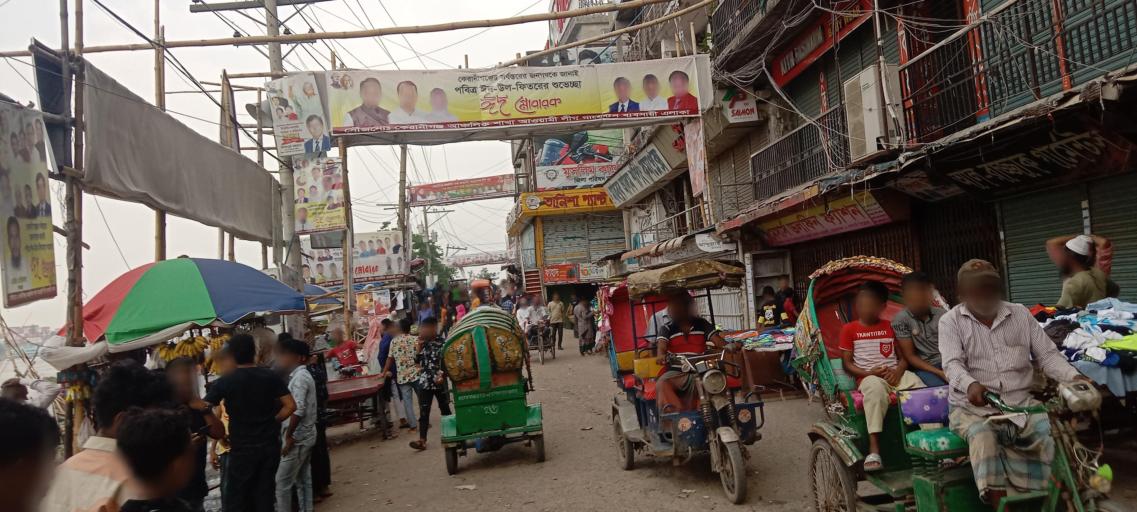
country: BD
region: Dhaka
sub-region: Dhaka
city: Dhaka
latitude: 23.7040
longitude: 90.4070
